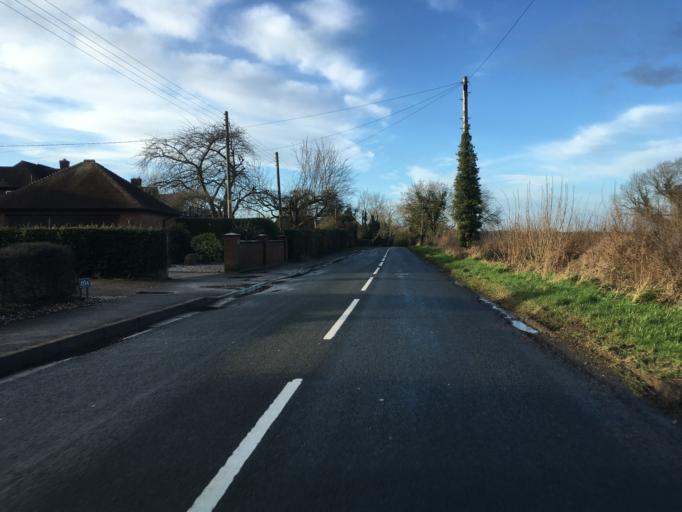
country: GB
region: England
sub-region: Warwickshire
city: Henley in Arden
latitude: 52.2244
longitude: -1.7742
